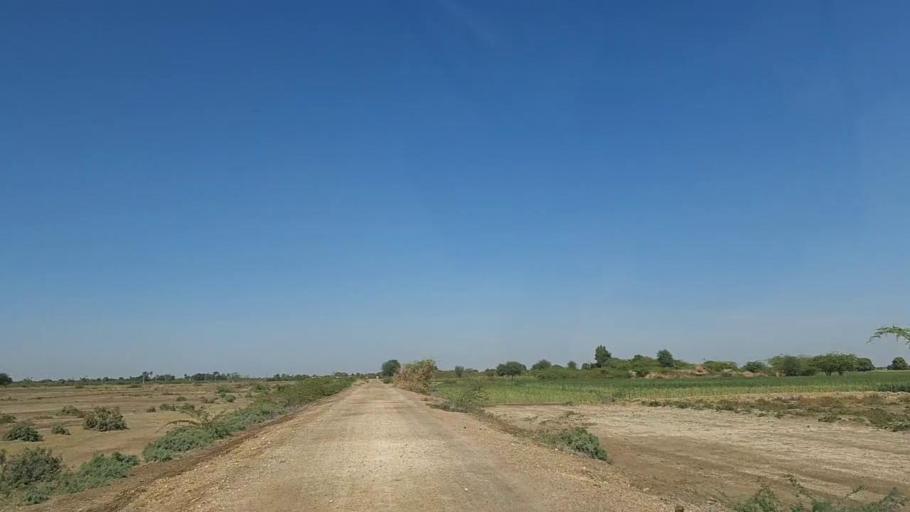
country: PK
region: Sindh
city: Samaro
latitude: 25.3078
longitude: 69.5148
